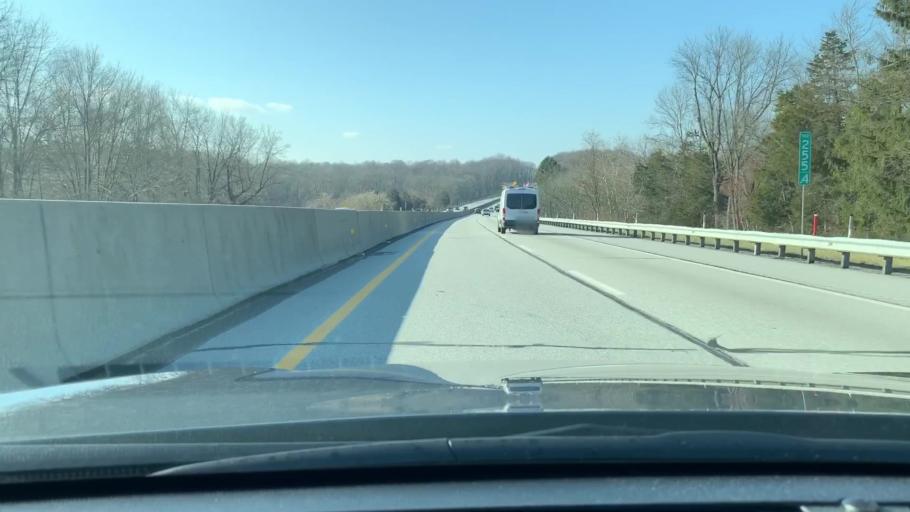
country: US
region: Pennsylvania
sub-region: Lancaster County
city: Elizabethtown
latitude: 40.2074
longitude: -76.6377
